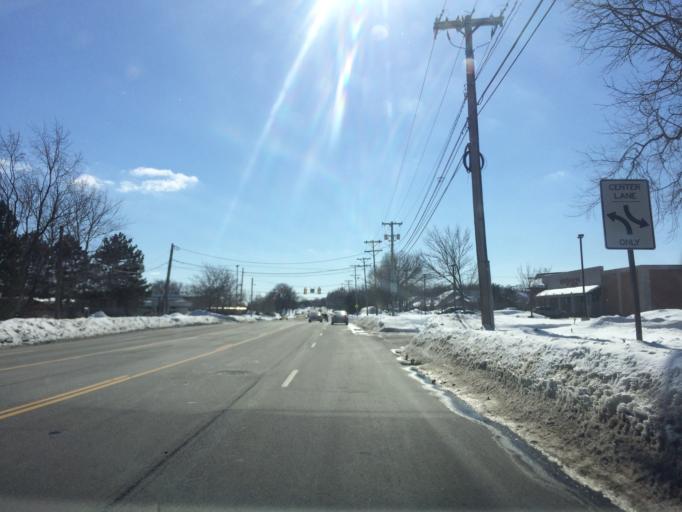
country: US
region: New York
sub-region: Monroe County
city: Rochester
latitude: 43.1269
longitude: -77.5923
